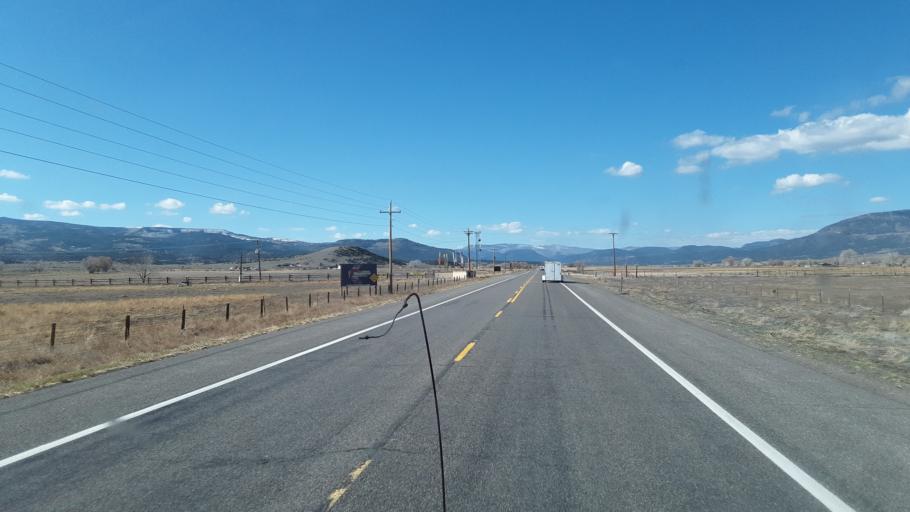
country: US
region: Colorado
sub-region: Rio Grande County
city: Del Norte
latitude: 37.6768
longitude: -106.4492
